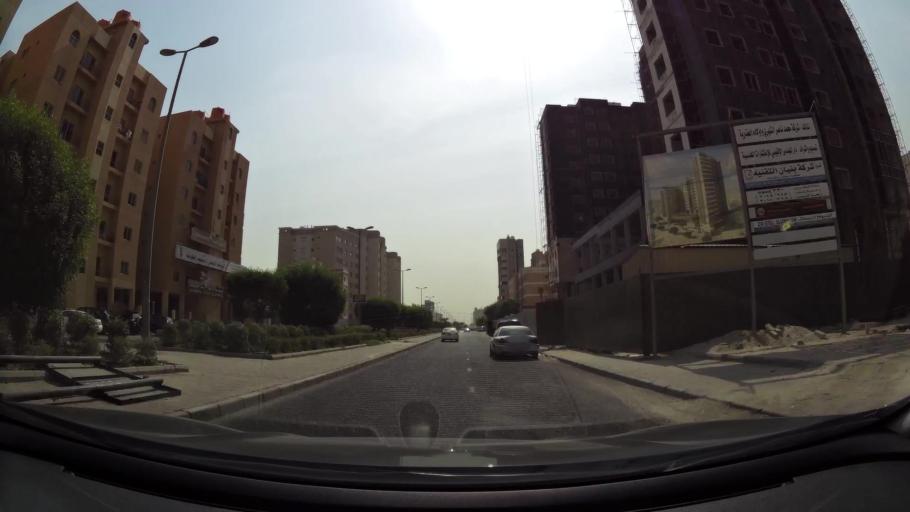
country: KW
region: Al Asimah
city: Ar Rabiyah
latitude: 29.3084
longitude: 47.9146
